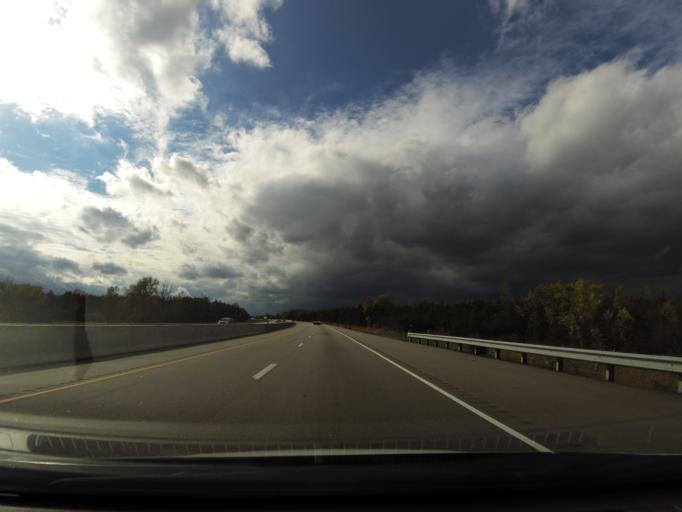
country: CA
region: Ontario
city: Belleville
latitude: 44.2218
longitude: -77.2828
